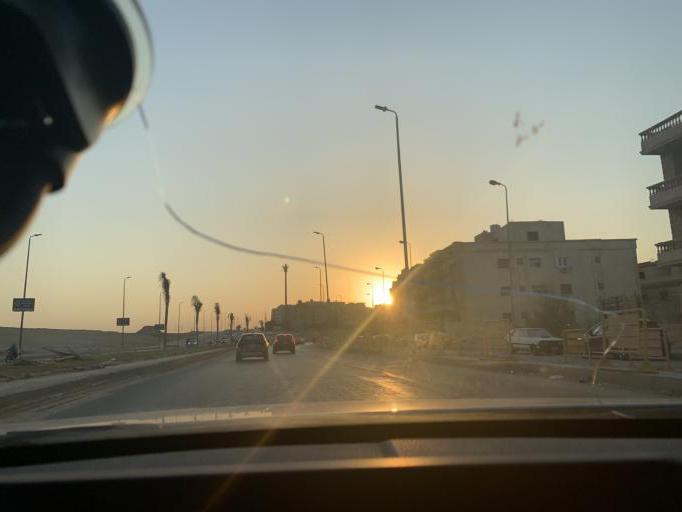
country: EG
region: Muhafazat al Qahirah
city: Cairo
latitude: 29.9994
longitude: 31.4656
